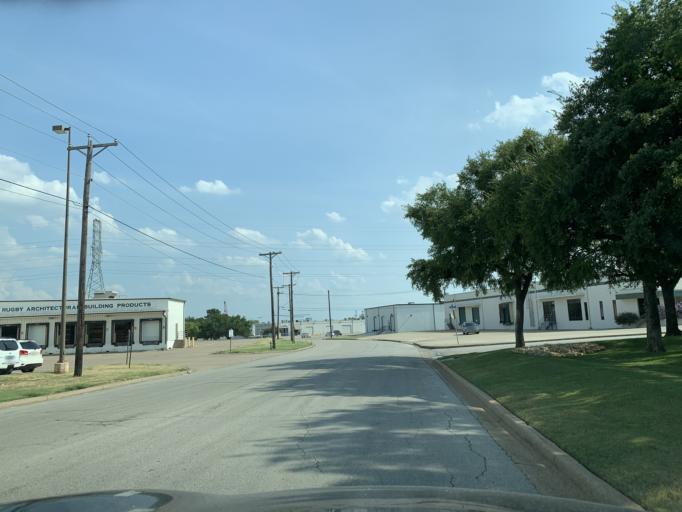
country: US
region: Texas
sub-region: Tarrant County
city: Richland Hills
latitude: 32.8075
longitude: -97.2170
